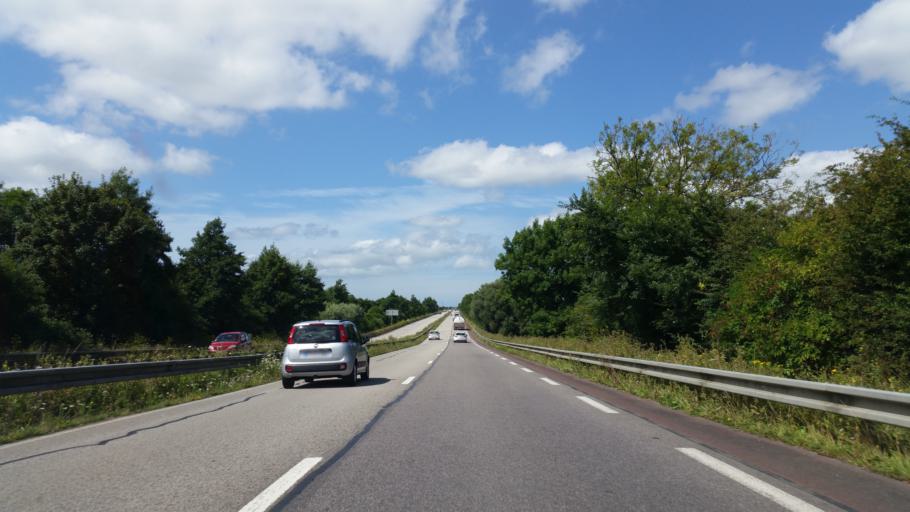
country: FR
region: Lower Normandy
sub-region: Departement de la Manche
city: Sainte-Mere-Eglise
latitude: 49.4312
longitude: -1.3351
